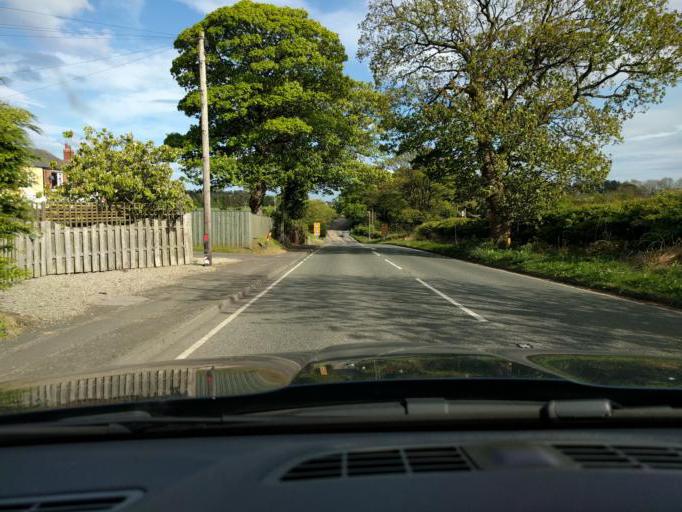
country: GB
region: England
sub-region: Northumberland
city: Morpeth
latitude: 55.1508
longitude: -1.6626
